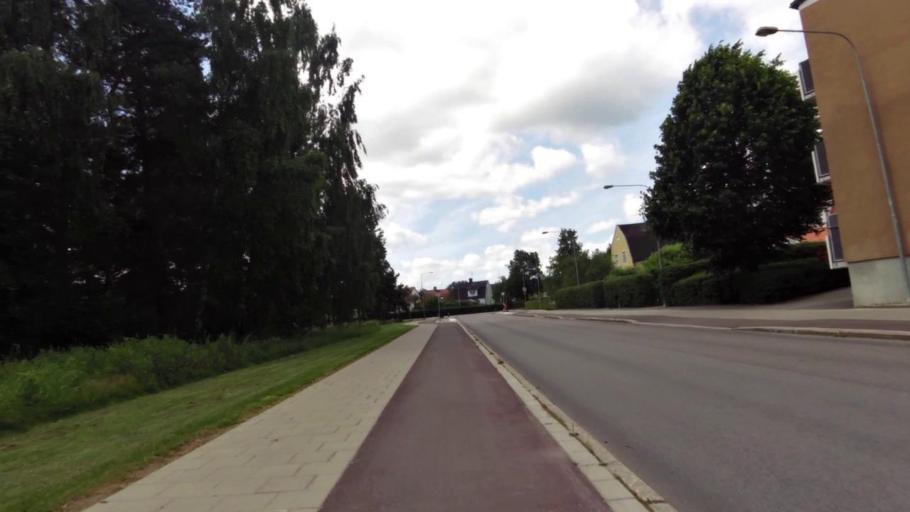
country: SE
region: OEstergoetland
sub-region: Linkopings Kommun
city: Linkoping
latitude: 58.4121
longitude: 15.5988
